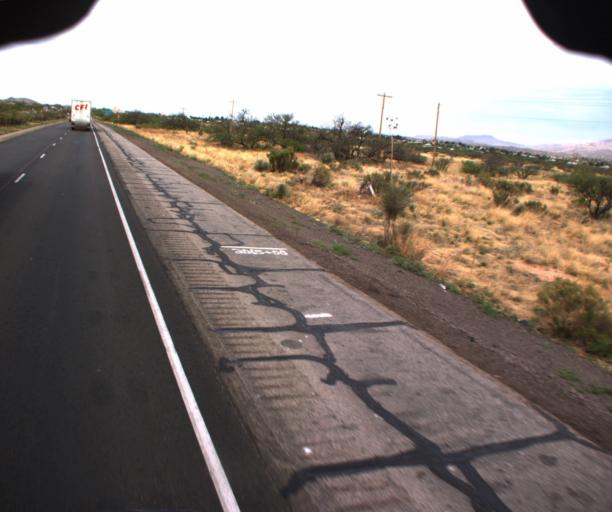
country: US
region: Arizona
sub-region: Cochise County
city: Mescal
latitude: 31.9632
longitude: -110.4152
